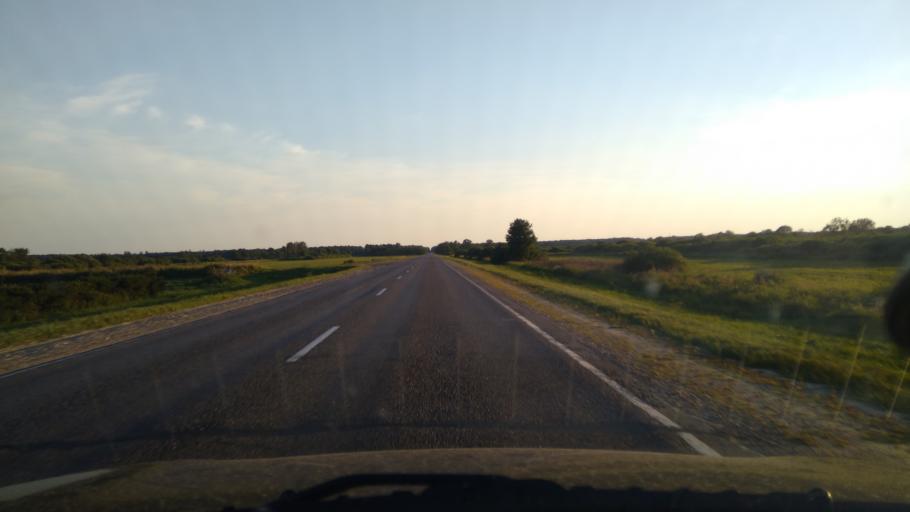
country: BY
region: Brest
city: Nyakhachava
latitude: 52.6242
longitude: 25.1654
